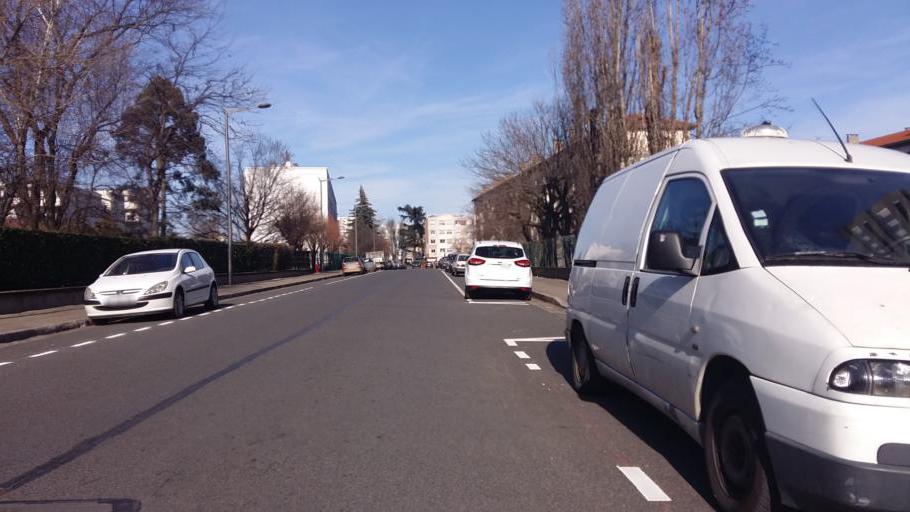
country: FR
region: Rhone-Alpes
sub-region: Departement du Rhone
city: Venissieux
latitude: 45.7270
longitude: 4.8802
